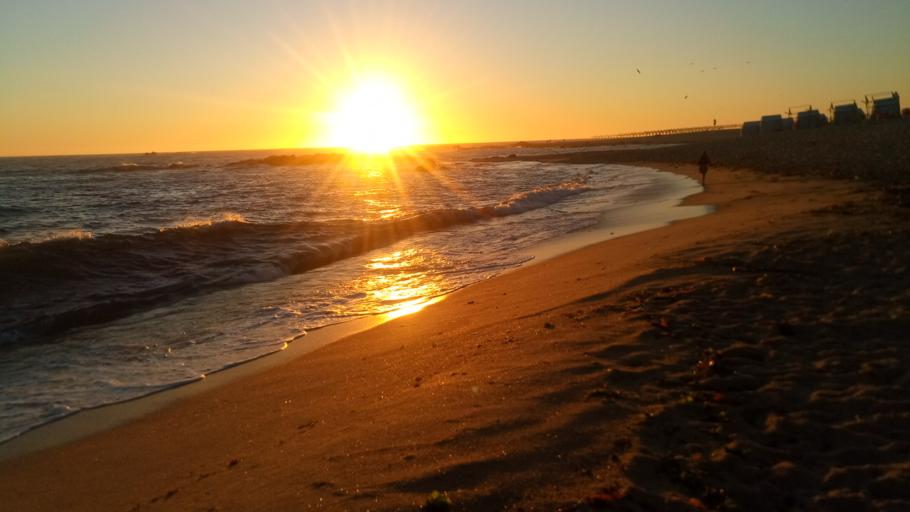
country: PT
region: Porto
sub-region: Povoa de Varzim
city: Aver-o-Mar
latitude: 41.3938
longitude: -8.7771
